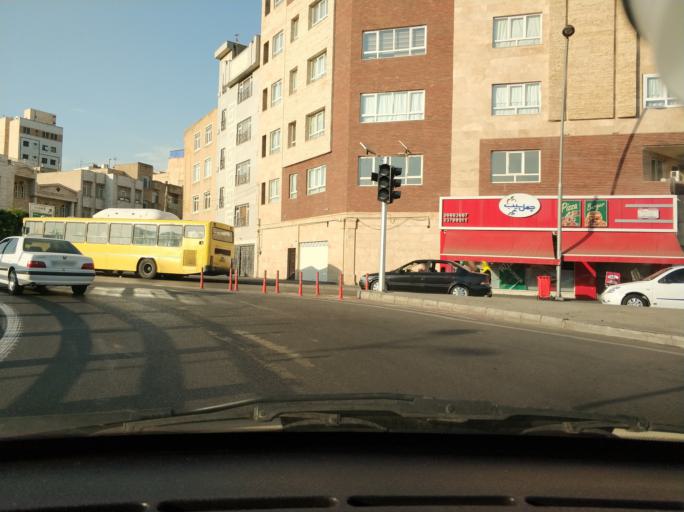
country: IR
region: Tehran
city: Tehran
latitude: 35.6874
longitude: 51.4579
